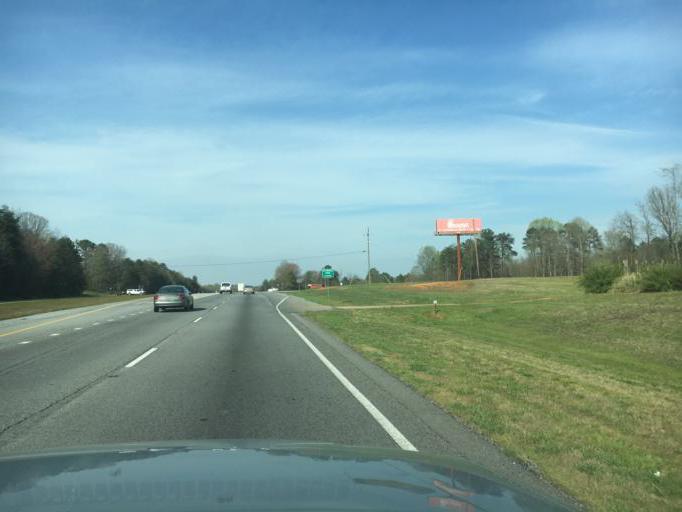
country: US
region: Georgia
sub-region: Habersham County
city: Raoul
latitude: 34.4566
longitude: -83.6096
